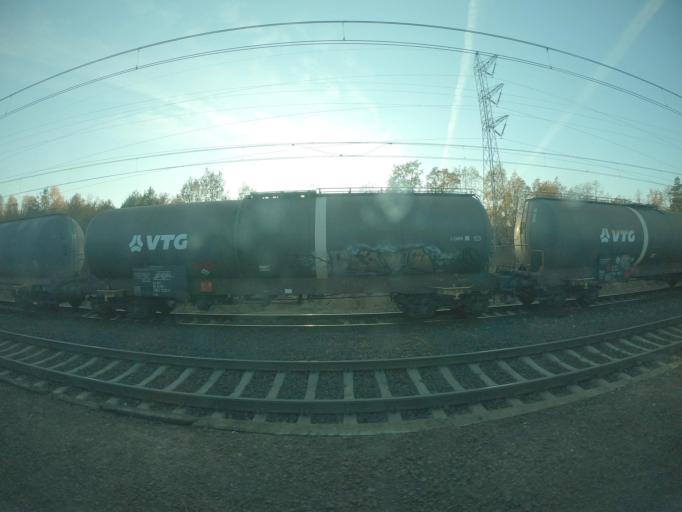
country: PL
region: Lubusz
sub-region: Powiat slubicki
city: Rzepin
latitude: 52.3068
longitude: 14.8672
